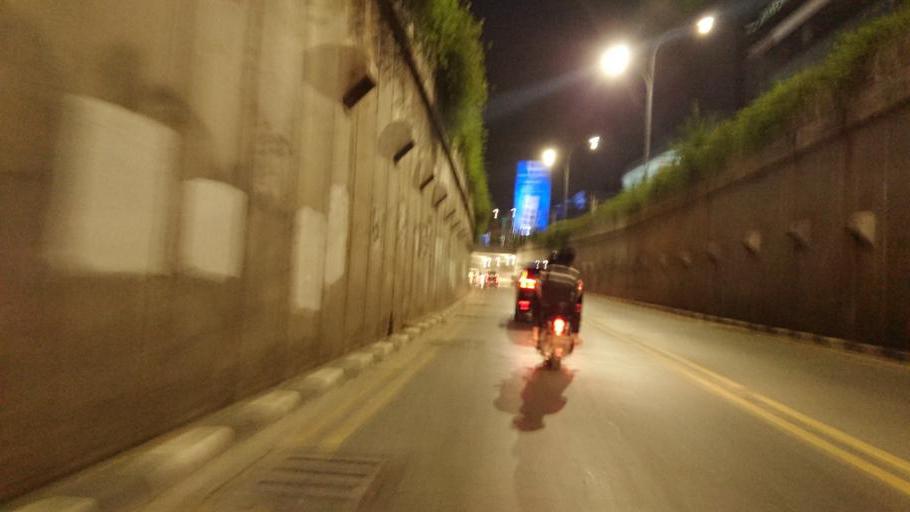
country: ID
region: Jakarta Raya
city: Jakarta
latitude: -6.2465
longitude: 106.7816
